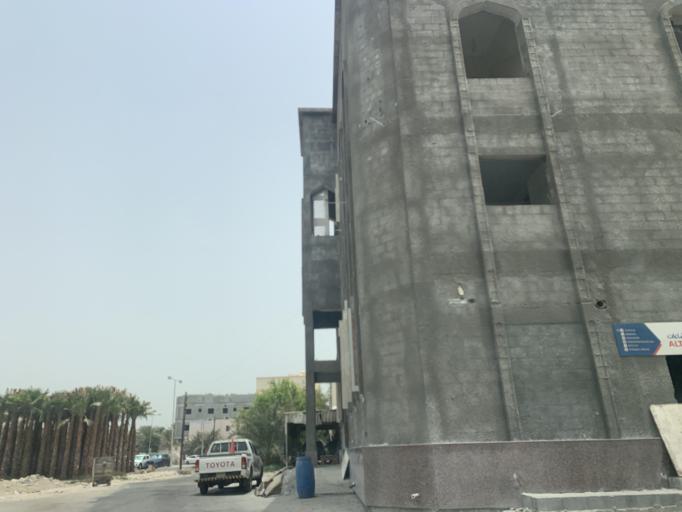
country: BH
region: Manama
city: Jidd Hafs
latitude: 26.2169
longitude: 50.5089
